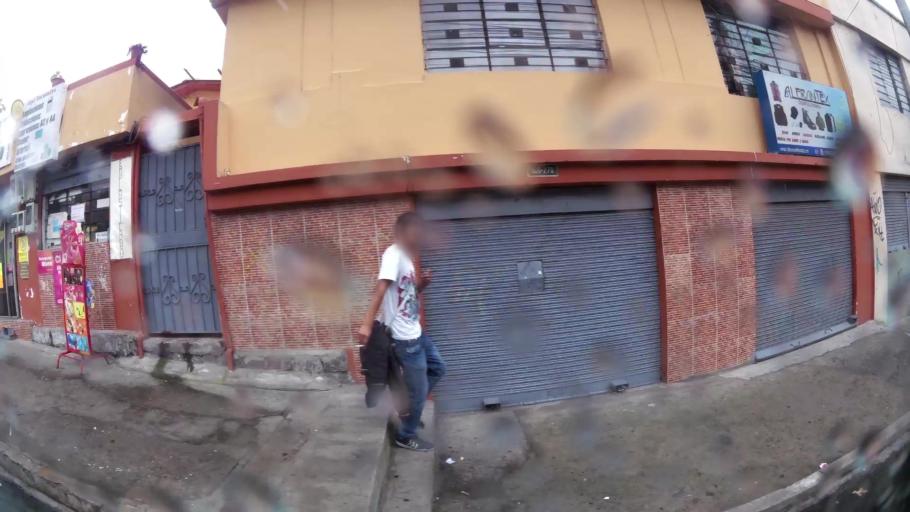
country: EC
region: Pichincha
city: Quito
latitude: -0.1236
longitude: -78.4980
